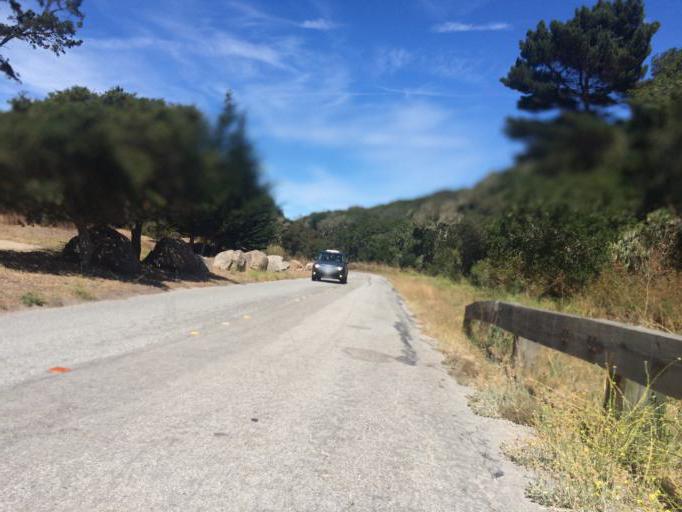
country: US
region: California
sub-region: Monterey County
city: Monterey
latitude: 36.5912
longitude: -121.8878
